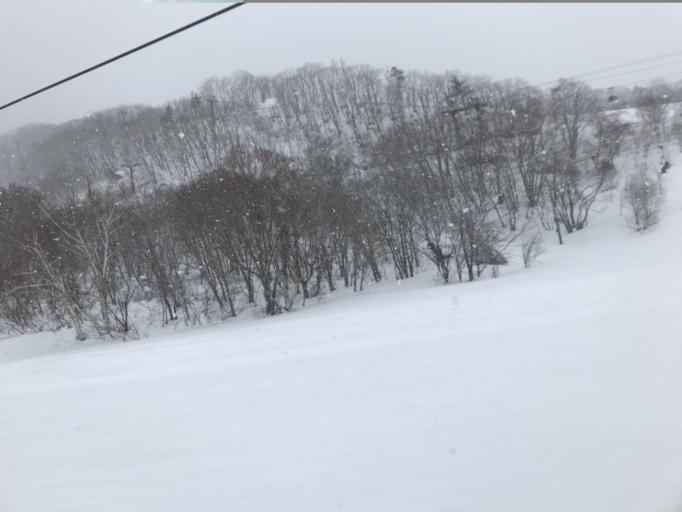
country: JP
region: Nagano
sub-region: Kitaazumi Gun
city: Hakuba
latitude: 36.7539
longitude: 137.8585
